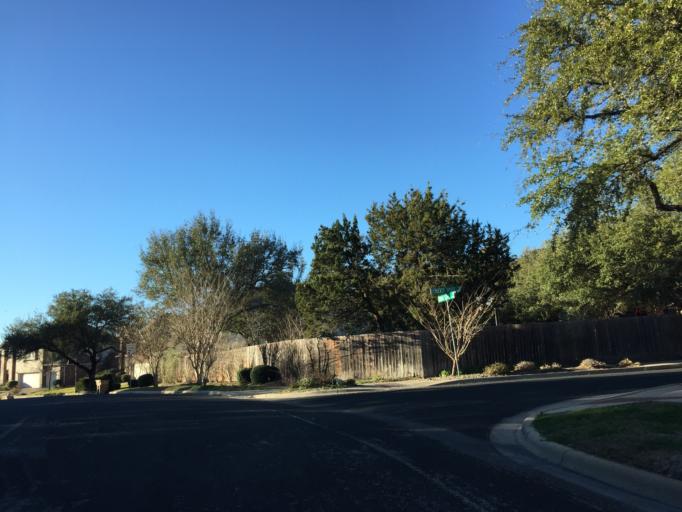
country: US
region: Texas
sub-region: Williamson County
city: Jollyville
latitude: 30.4343
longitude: -97.7855
